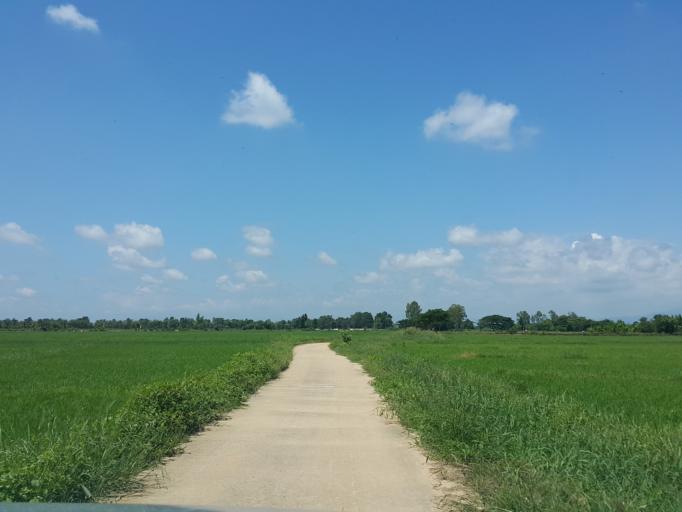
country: TH
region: Lamphun
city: Ban Thi
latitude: 18.6822
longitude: 99.1315
